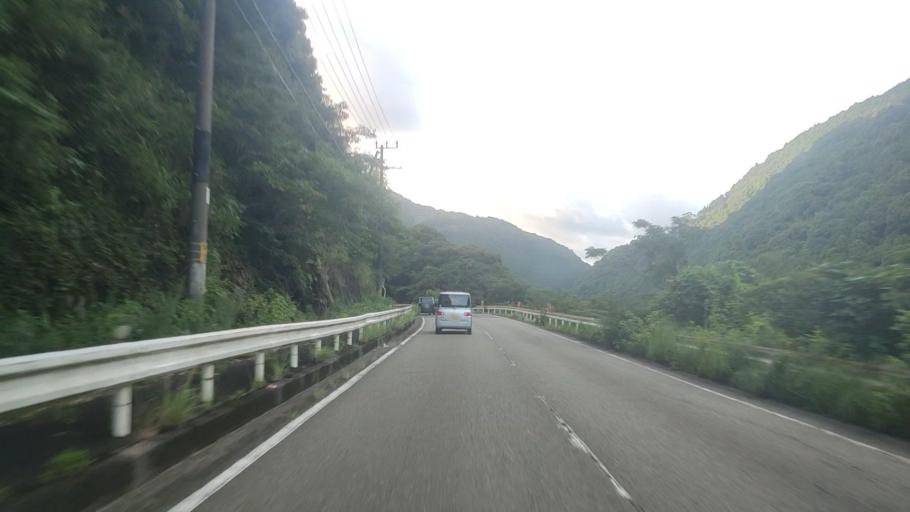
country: JP
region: Wakayama
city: Tanabe
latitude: 33.7651
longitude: 135.5002
